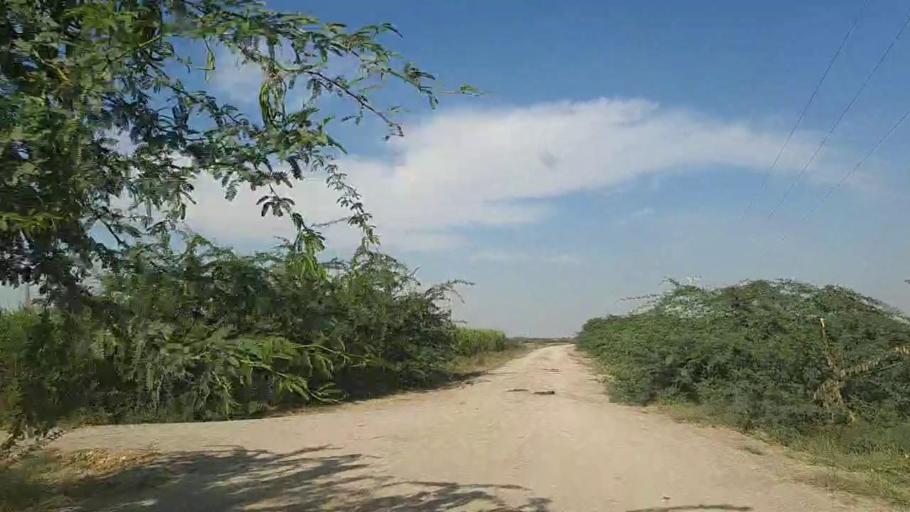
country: PK
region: Sindh
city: Bulri
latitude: 24.8319
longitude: 68.2725
